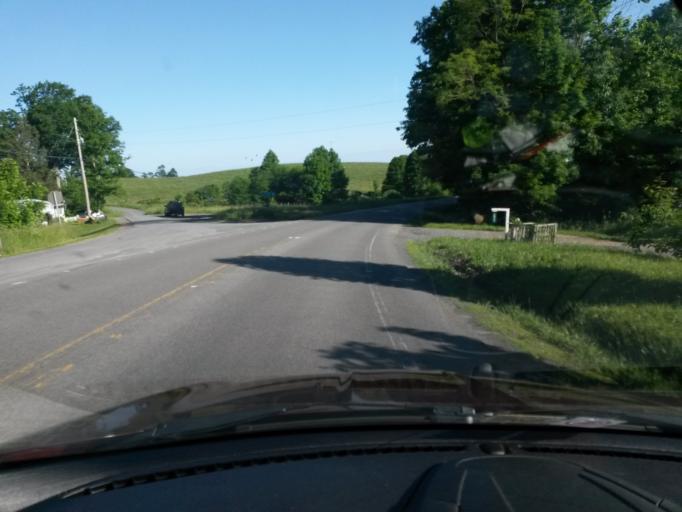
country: US
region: West Virginia
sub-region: Nicholas County
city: Craigsville
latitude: 38.2336
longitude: -80.7107
